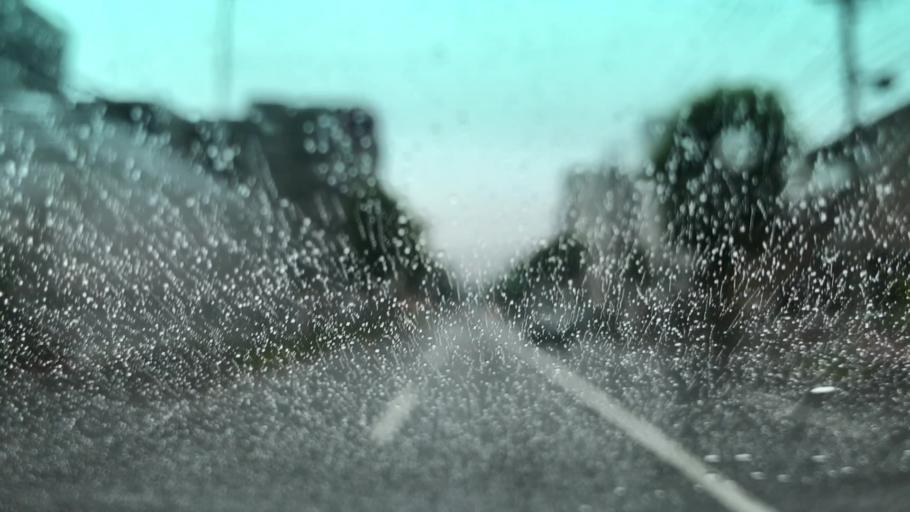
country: JP
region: Hokkaido
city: Sapporo
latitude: 43.0655
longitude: 141.3055
